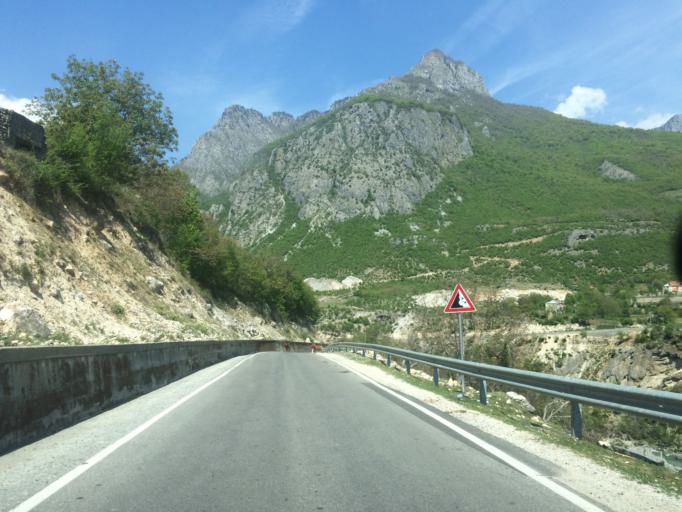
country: AL
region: Kukes
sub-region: Rrethi i Tropojes
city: Bajram Curri
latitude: 42.3857
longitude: 20.0771
